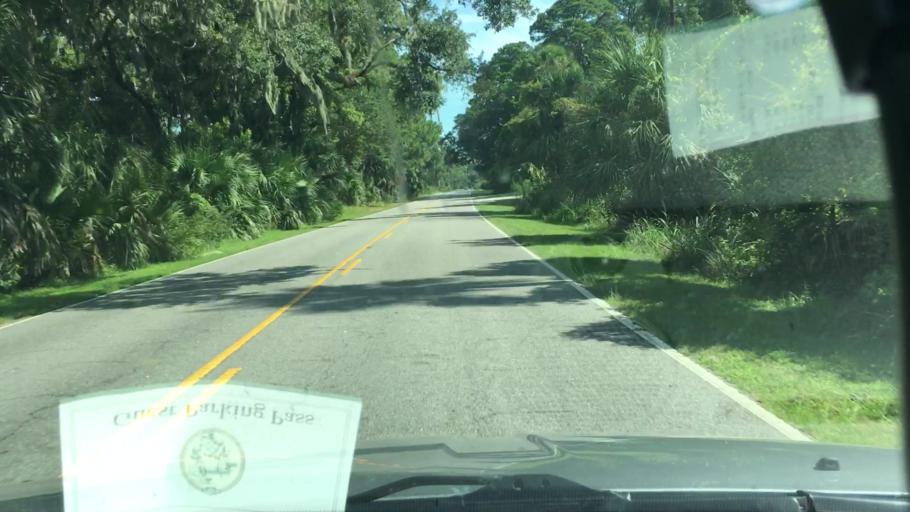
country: US
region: South Carolina
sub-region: Beaufort County
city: Beaufort
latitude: 32.3794
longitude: -80.4446
